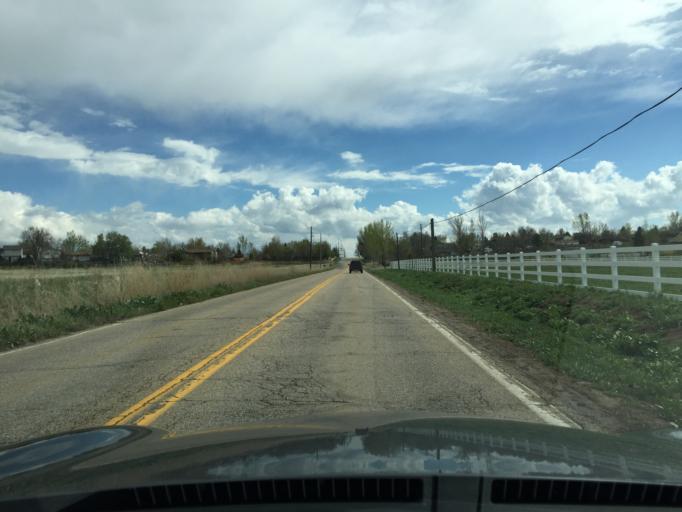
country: US
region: Colorado
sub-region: Boulder County
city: Lafayette
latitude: 40.0136
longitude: -105.0933
